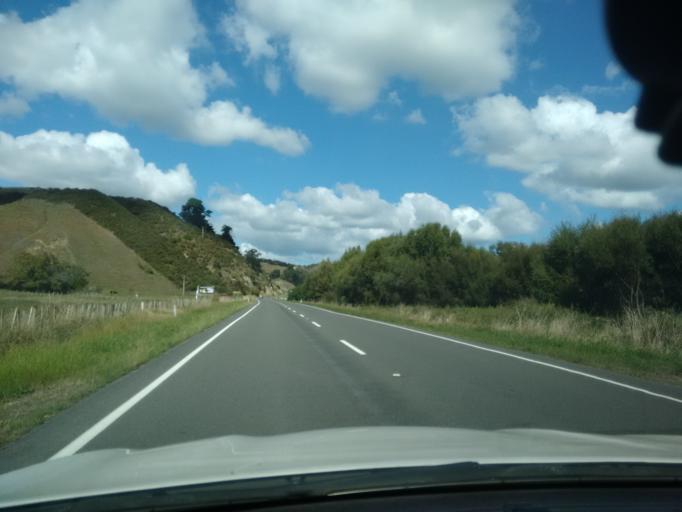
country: NZ
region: Manawatu-Wanganui
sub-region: Wanganui District
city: Wanganui
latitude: -39.8858
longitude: 175.1056
